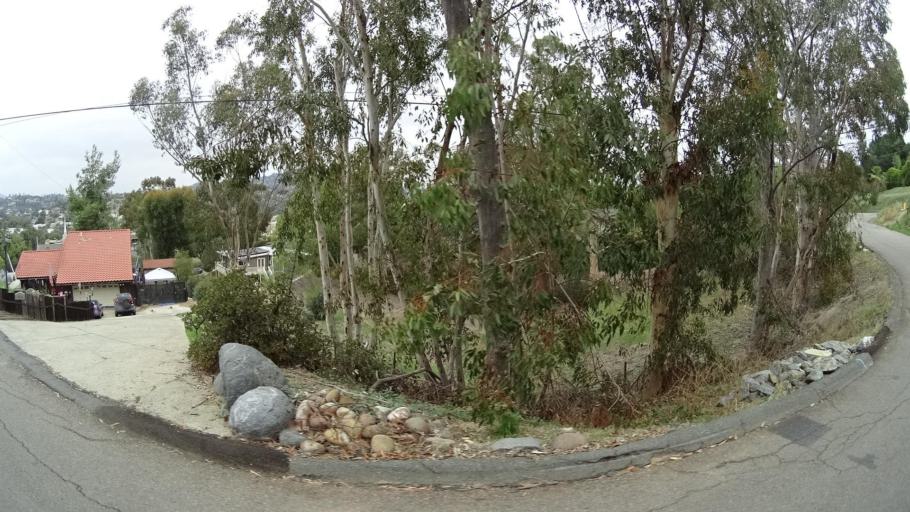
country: US
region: California
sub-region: San Diego County
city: Spring Valley
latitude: 32.7375
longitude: -116.9980
